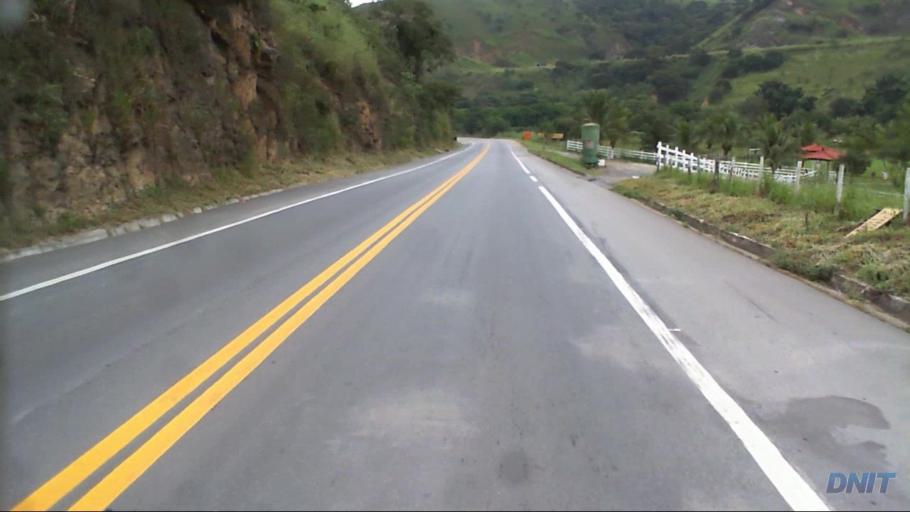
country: BR
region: Minas Gerais
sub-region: Timoteo
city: Timoteo
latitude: -19.6180
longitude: -42.7810
